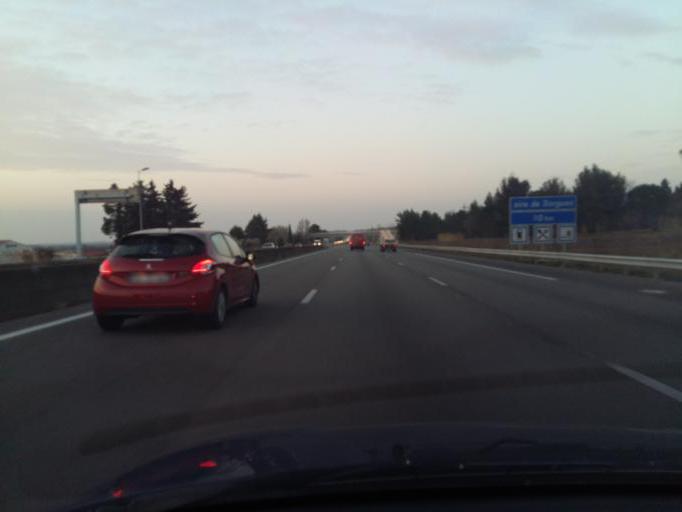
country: FR
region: Provence-Alpes-Cote d'Azur
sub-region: Departement du Vaucluse
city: Morieres-les-Avignon
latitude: 43.9272
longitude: 4.9132
